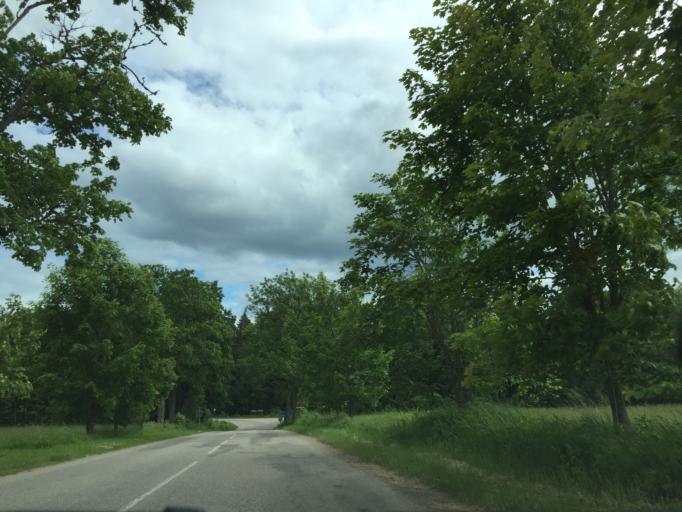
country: LV
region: Apes Novads
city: Ape
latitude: 57.4991
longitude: 26.4026
